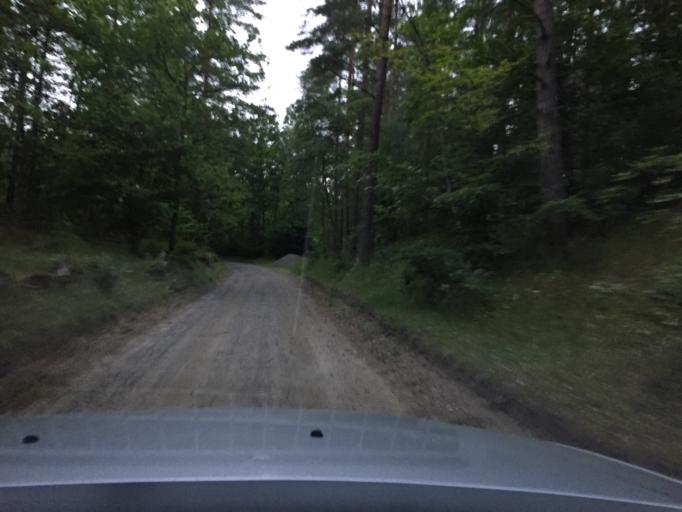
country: SE
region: Skane
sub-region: Kristianstads Kommun
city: Degeberga
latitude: 55.7299
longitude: 14.1237
